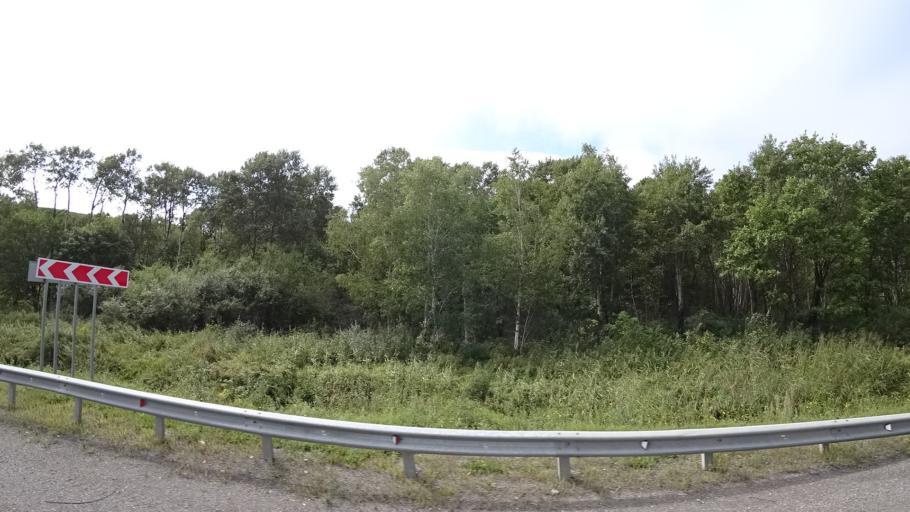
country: RU
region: Primorskiy
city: Lyalichi
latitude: 44.1100
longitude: 132.4198
